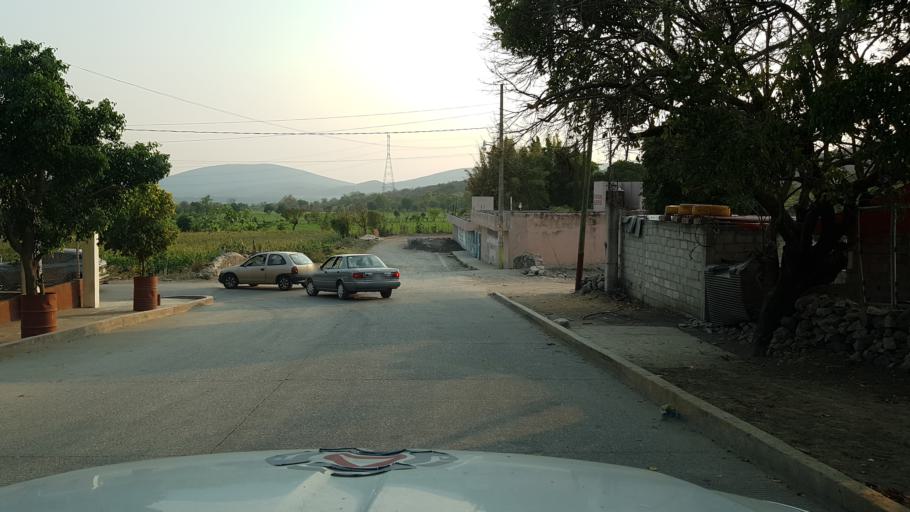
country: MX
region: Morelos
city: Anenecuilco
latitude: 18.7616
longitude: -98.9874
